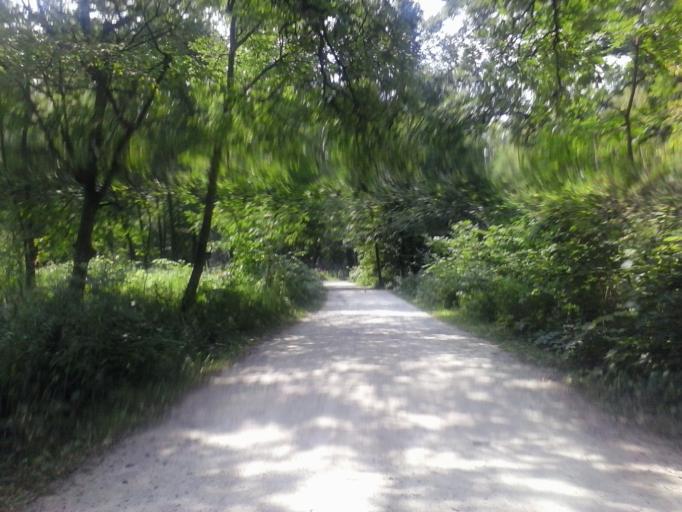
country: US
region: Illinois
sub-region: DuPage County
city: Lisle
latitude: 41.8204
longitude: -88.1048
